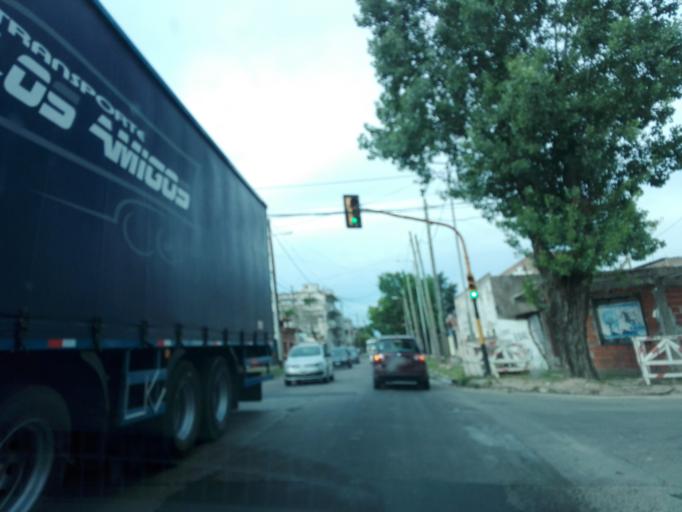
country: AR
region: Buenos Aires
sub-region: Partido de Avellaneda
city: Avellaneda
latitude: -34.6882
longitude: -58.3506
